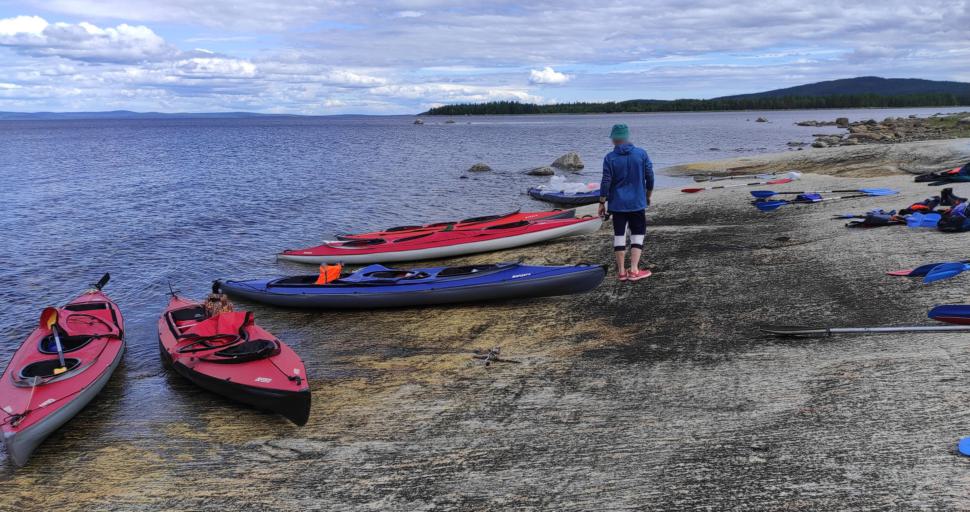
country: RU
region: Murmansk
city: Poyakonda
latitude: 66.7758
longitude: 32.7445
